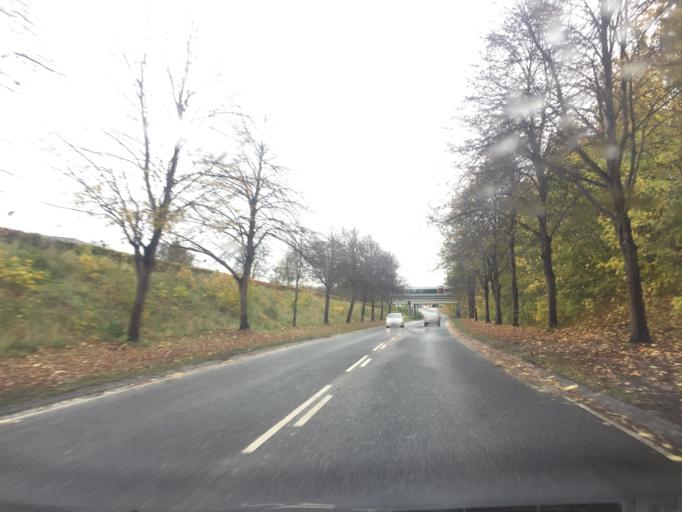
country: DK
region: Capital Region
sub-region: Fredensborg Kommune
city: Humlebaek
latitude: 55.9636
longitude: 12.5295
